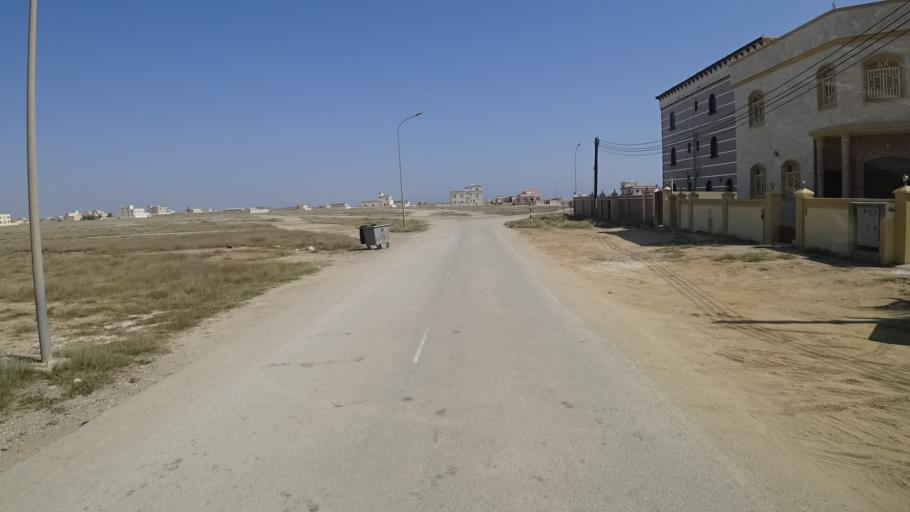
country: OM
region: Zufar
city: Salalah
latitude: 16.9850
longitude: 54.7102
